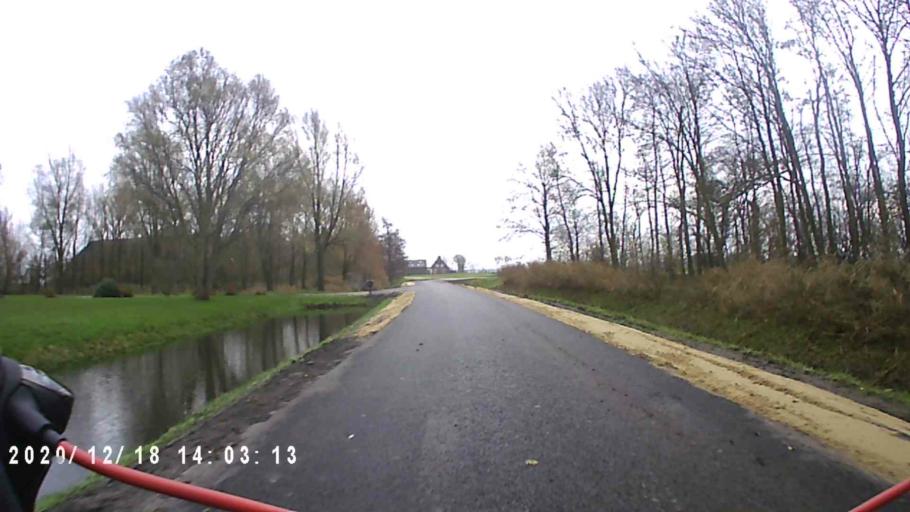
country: NL
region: Groningen
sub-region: Gemeente Bedum
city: Bedum
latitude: 53.2942
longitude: 6.6487
